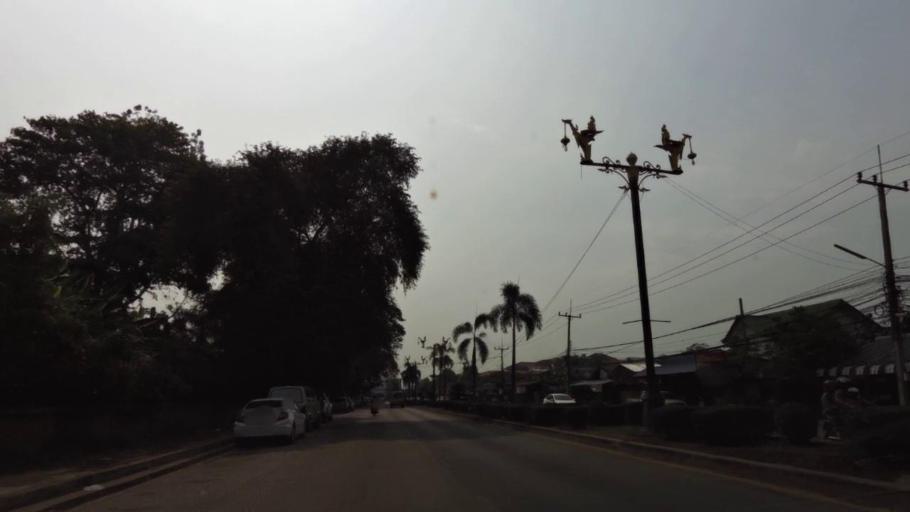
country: TH
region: Phra Nakhon Si Ayutthaya
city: Phra Nakhon Si Ayutthaya
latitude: 14.3471
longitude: 100.5666
